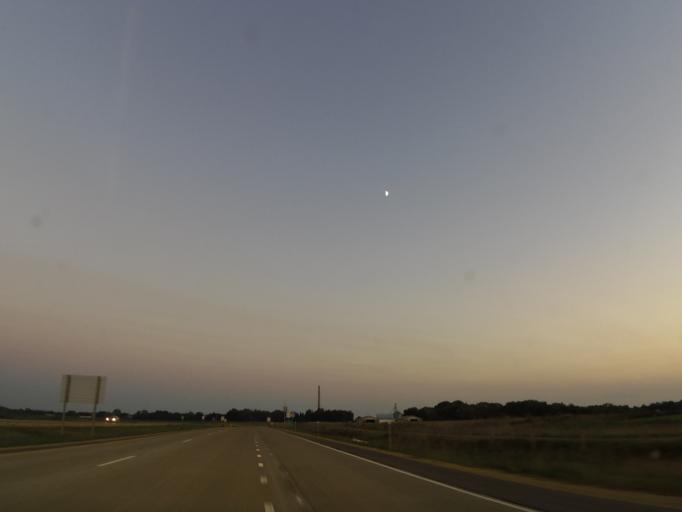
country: US
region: Minnesota
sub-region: Washington County
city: Oak Park Heights
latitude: 45.0542
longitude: -92.7795
